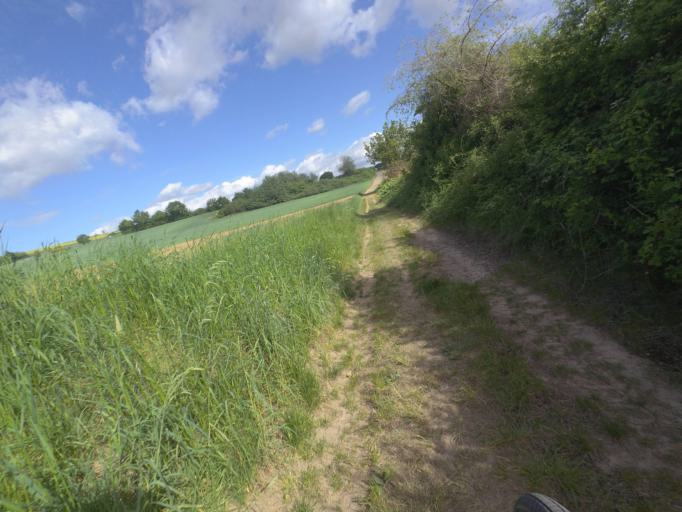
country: DE
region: Rheinland-Pfalz
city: Kirchheimbolanden
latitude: 49.6741
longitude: 8.0065
